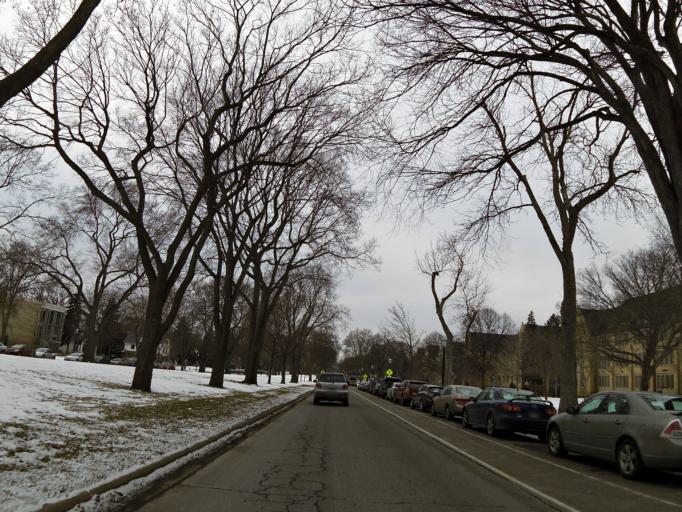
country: US
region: Minnesota
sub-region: Ramsey County
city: Falcon Heights
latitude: 44.9417
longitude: -93.1880
